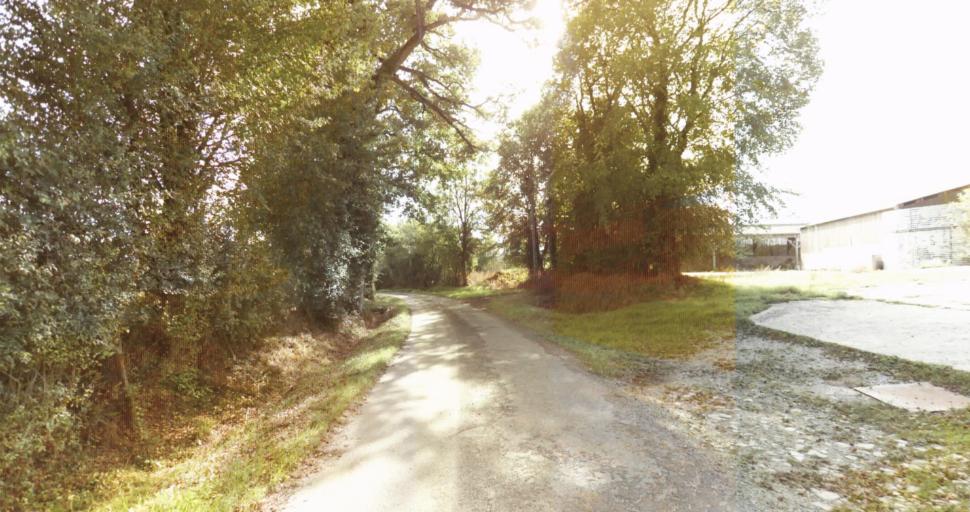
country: FR
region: Lower Normandy
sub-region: Departement de l'Orne
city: Gace
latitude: 48.7185
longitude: 0.2443
